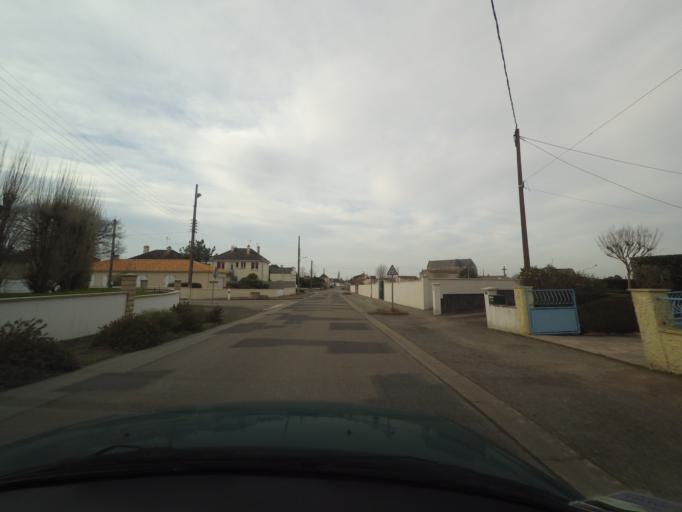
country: FR
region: Pays de la Loire
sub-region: Departement de la Loire-Atlantique
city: Saint-Pere-en-Retz
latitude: 47.2033
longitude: -2.0413
